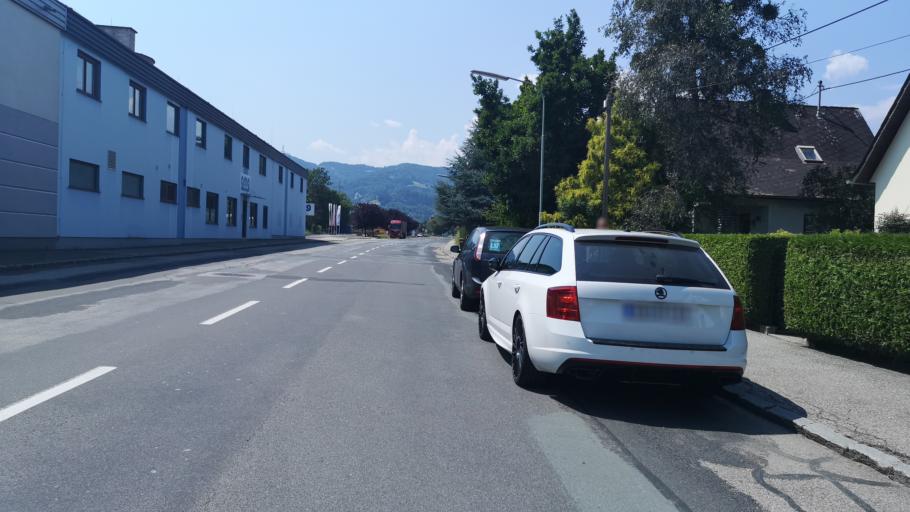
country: AT
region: Styria
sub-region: Politischer Bezirk Deutschlandsberg
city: Deutschlandsberg
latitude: 46.8222
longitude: 15.2349
